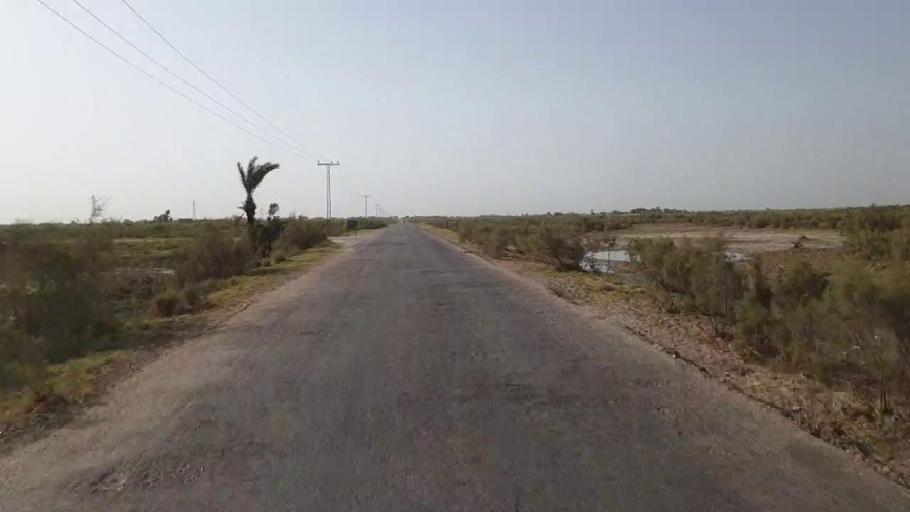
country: PK
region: Sindh
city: Khadro
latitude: 26.3478
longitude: 68.9238
